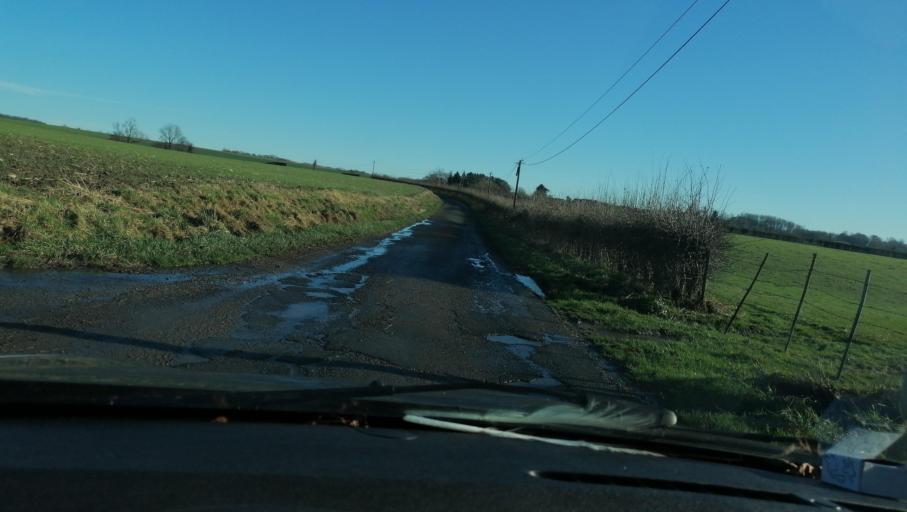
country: FR
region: Nord-Pas-de-Calais
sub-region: Departement du Nord
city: Ferriere-la-Grande
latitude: 50.2178
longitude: 4.0370
